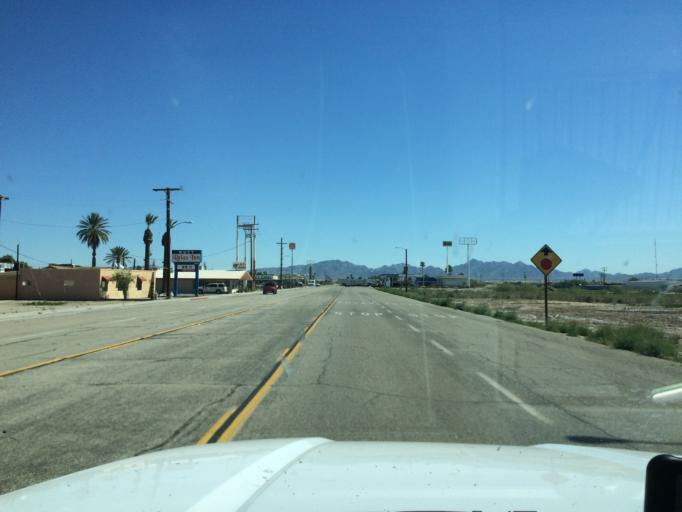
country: US
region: California
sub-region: Riverside County
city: Blythe
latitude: 33.6108
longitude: -114.5736
